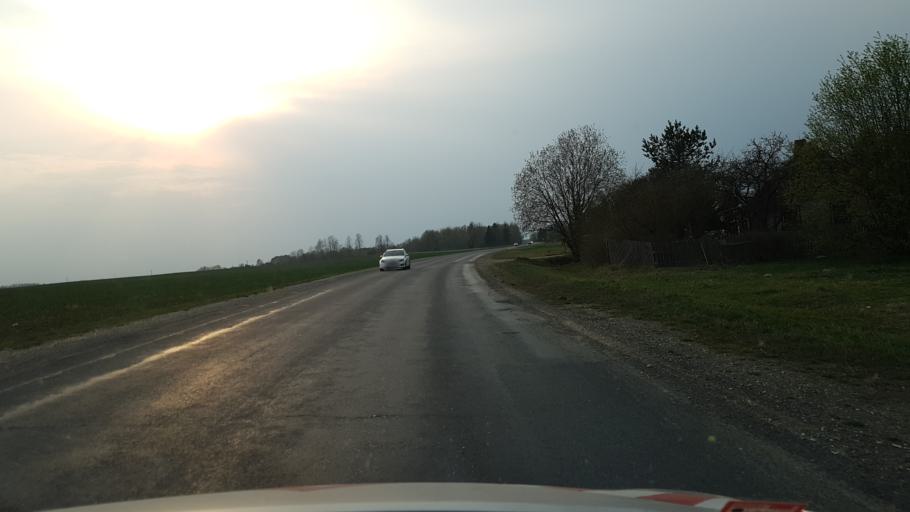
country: EE
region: Harju
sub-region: Raasiku vald
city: Arukula
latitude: 59.3442
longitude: 25.1098
